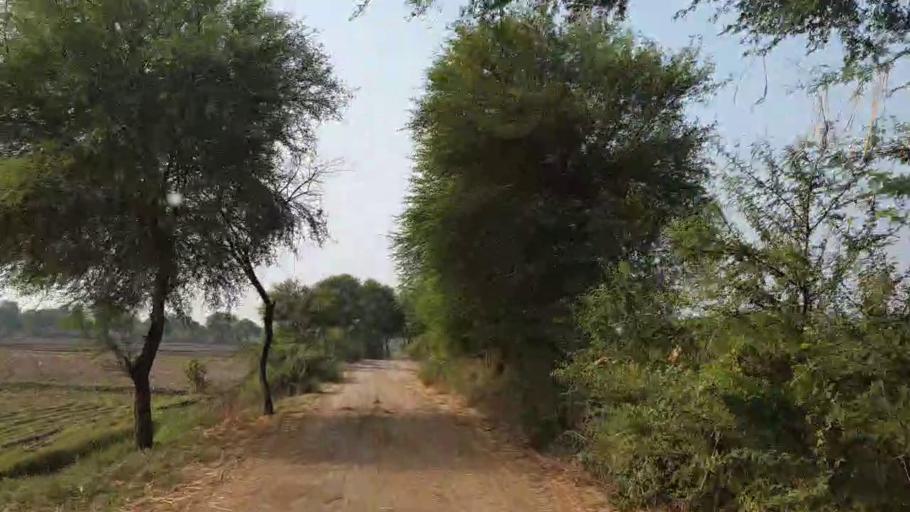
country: PK
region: Sindh
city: Matli
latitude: 25.0695
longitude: 68.6104
